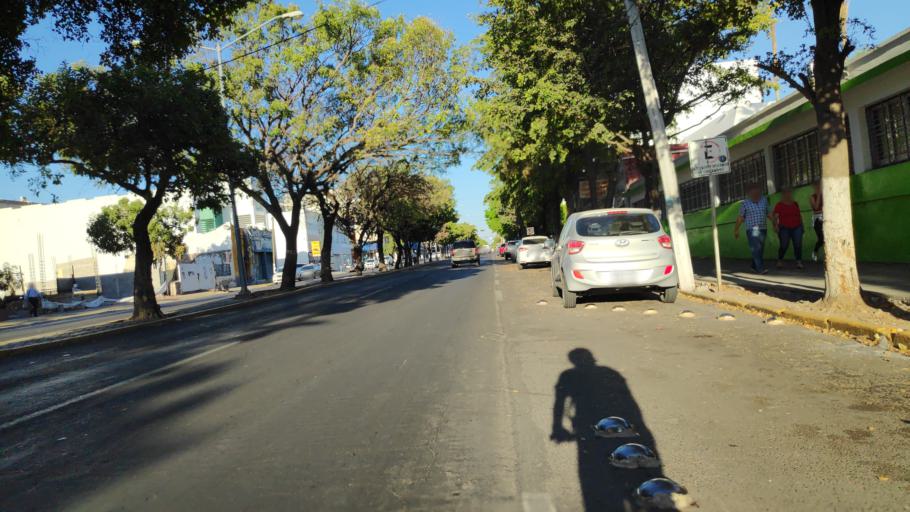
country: MX
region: Sinaloa
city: Culiacan
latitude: 24.8043
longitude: -107.3975
